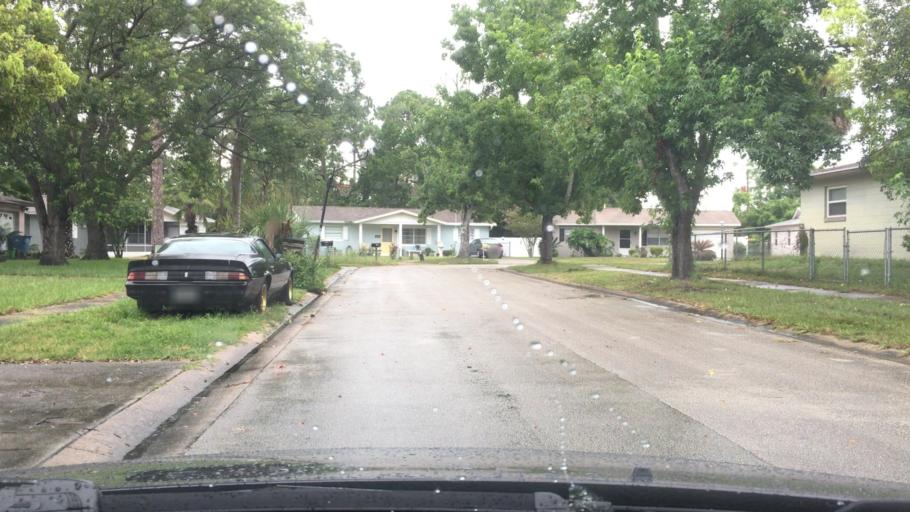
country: US
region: Florida
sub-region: Volusia County
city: Ormond Beach
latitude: 29.2522
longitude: -81.0785
